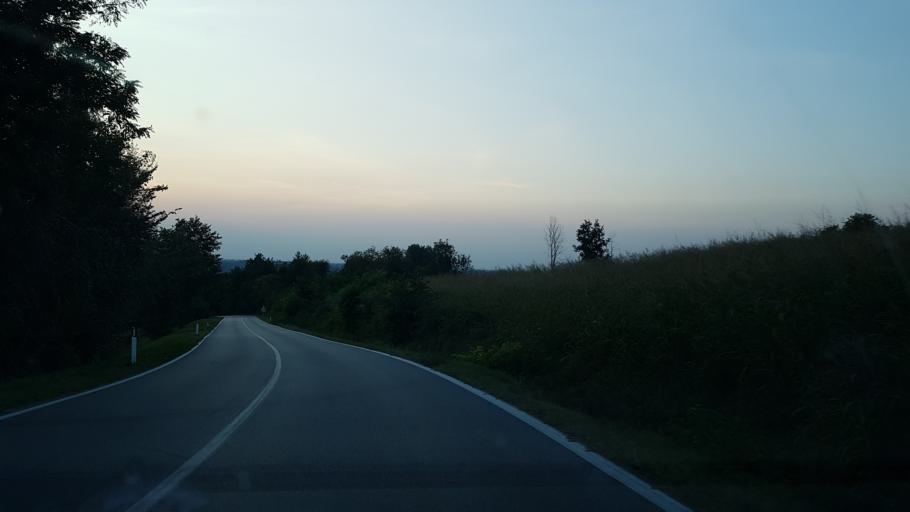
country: IT
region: Piedmont
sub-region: Provincia di Cuneo
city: Novello
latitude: 44.5863
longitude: 7.9154
